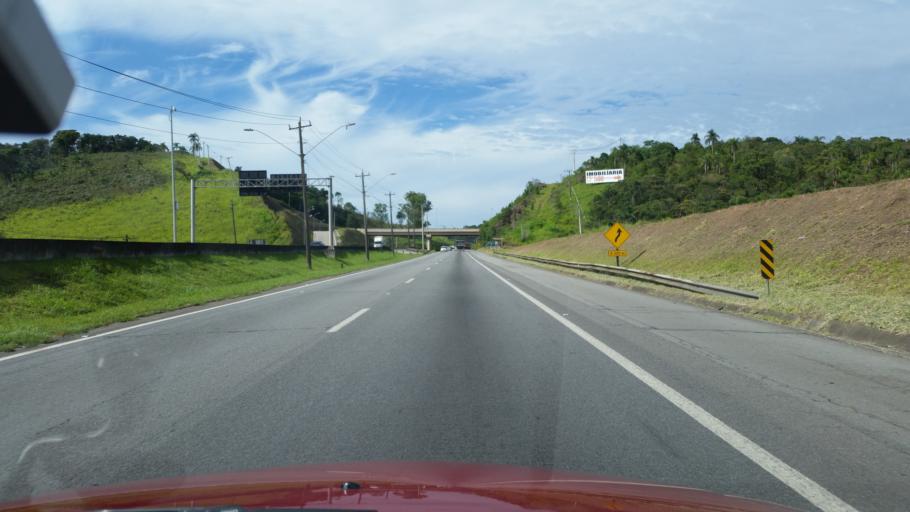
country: BR
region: Sao Paulo
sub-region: Sao Lourenco Da Serra
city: Sao Lourenco da Serra
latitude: -23.7993
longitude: -46.9158
